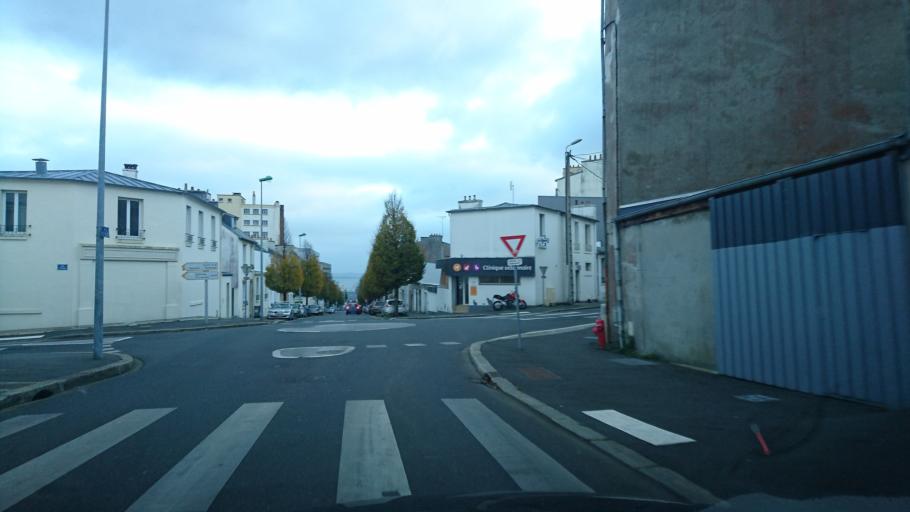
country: FR
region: Brittany
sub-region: Departement du Finistere
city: Brest
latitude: 48.3935
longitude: -4.4745
